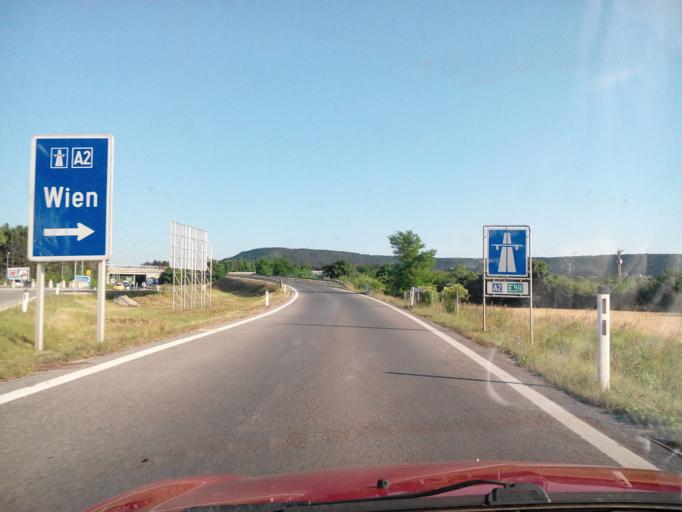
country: AT
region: Lower Austria
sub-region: Politischer Bezirk Wiener Neustadt
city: Theresienfeld
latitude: 47.8559
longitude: 16.1879
